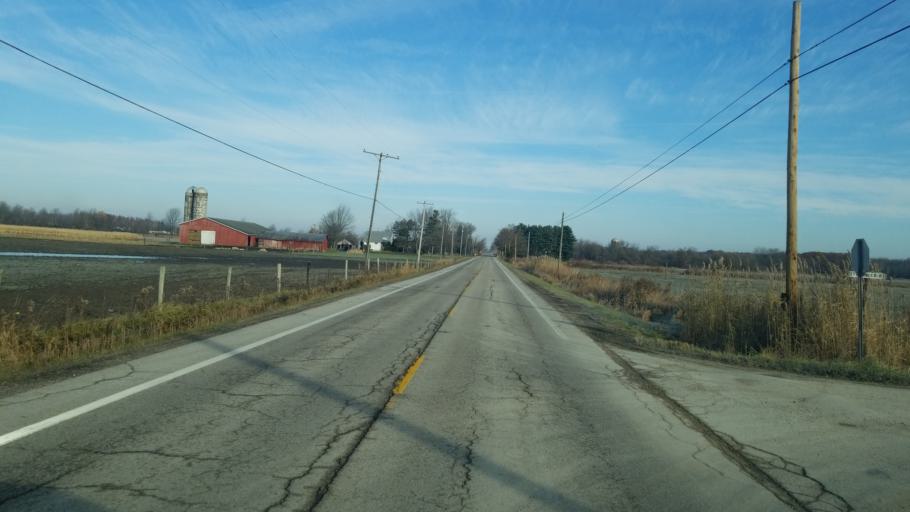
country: US
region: Ohio
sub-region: Ashtabula County
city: Jefferson
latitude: 41.7657
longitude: -80.6680
